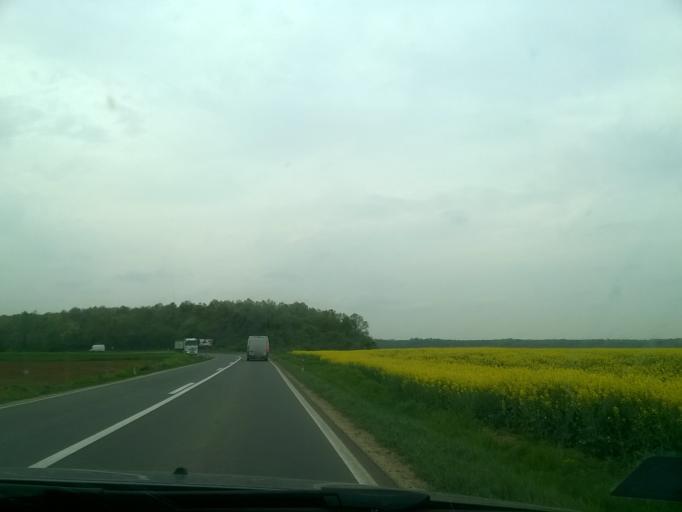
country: RS
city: Platicevo
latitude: 44.8450
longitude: 19.7674
